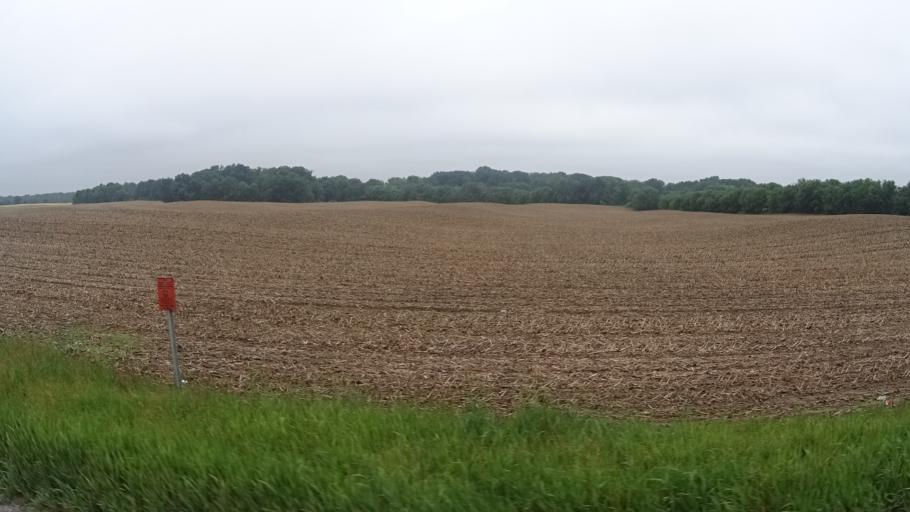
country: US
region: Ohio
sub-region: Erie County
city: Huron
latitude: 41.3558
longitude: -82.5755
